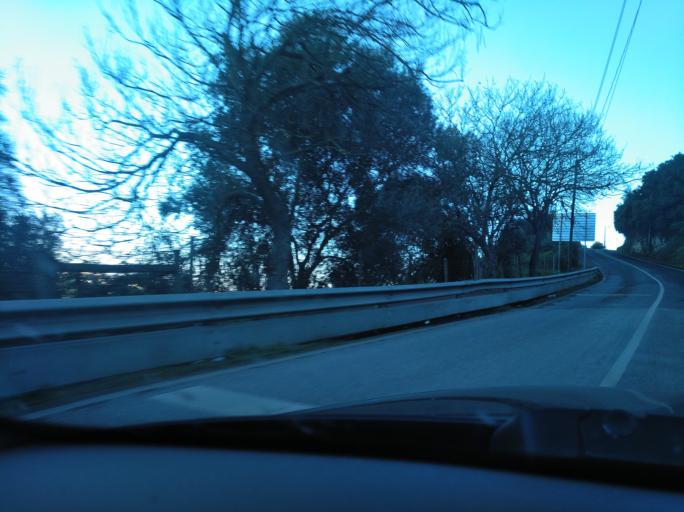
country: PT
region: Lisbon
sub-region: Loures
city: Unhos
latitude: 38.8217
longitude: -9.1216
